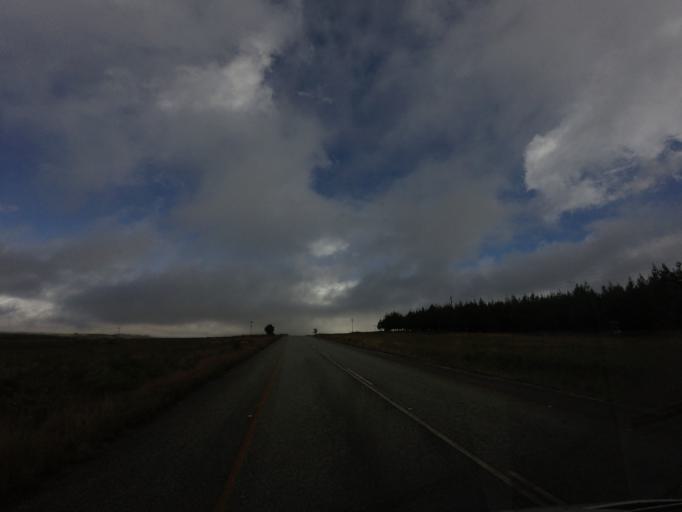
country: ZA
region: Mpumalanga
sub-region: Ehlanzeni District
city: Graksop
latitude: -24.8560
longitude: 30.8752
